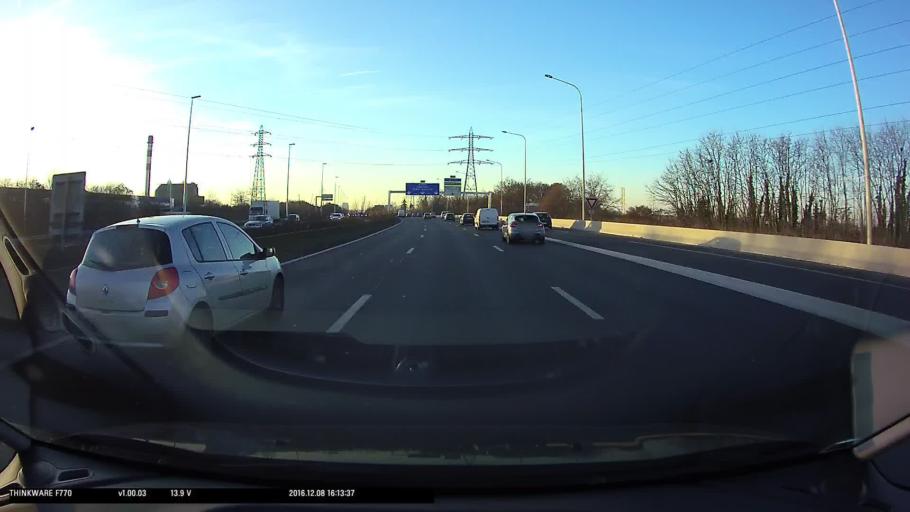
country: FR
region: Ile-de-France
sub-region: Departement du Val-d'Oise
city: Saint-Ouen-l'Aumone
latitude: 49.0309
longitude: 2.1223
